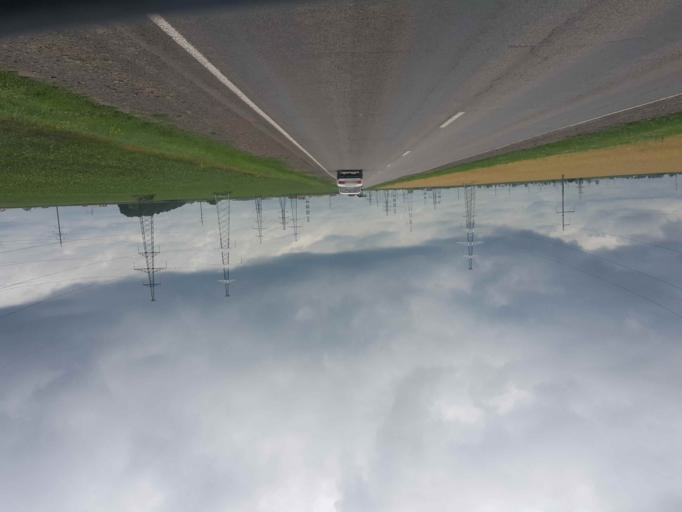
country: RU
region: Tambov
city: Komsomolets
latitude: 52.7770
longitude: 41.3434
